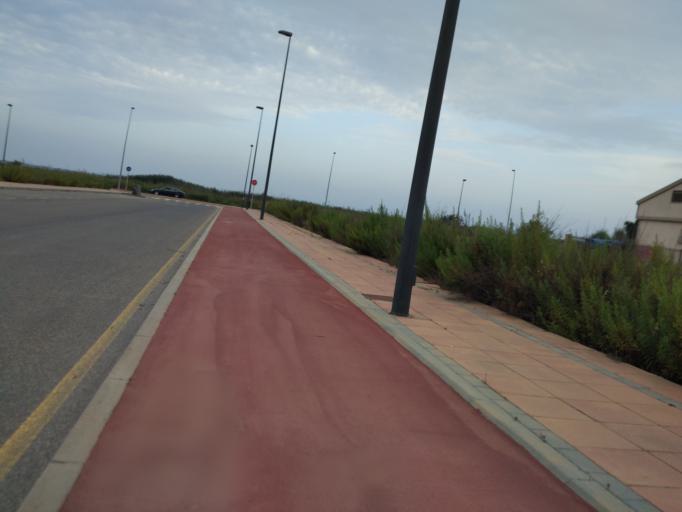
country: ES
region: Murcia
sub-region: Murcia
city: Los Alcazares
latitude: 37.7222
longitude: -0.8623
